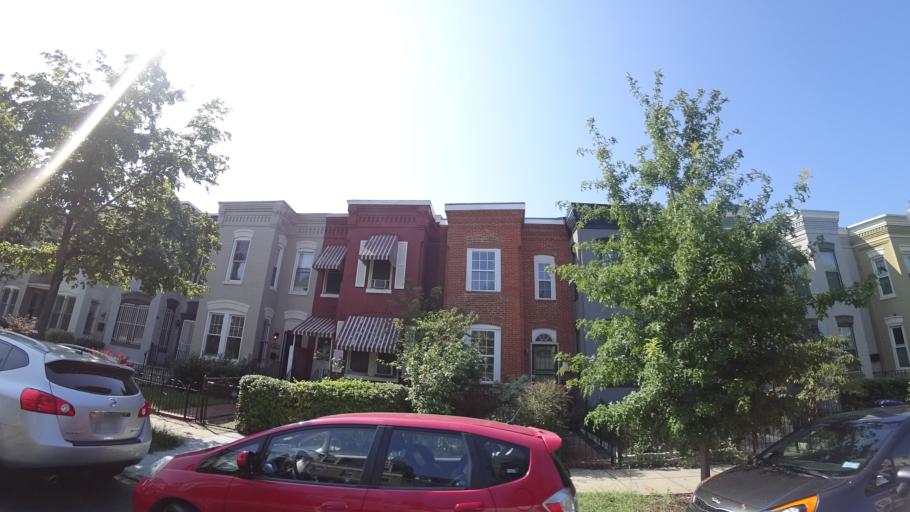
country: US
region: Maryland
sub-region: Prince George's County
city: Mount Rainier
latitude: 38.9014
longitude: -76.9892
